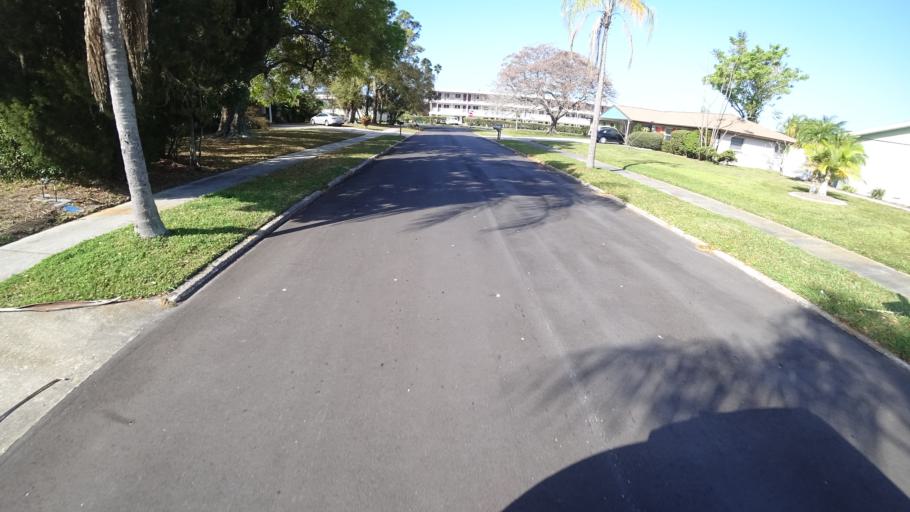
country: US
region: Florida
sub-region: Manatee County
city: Whitfield
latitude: 27.4132
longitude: -82.5708
